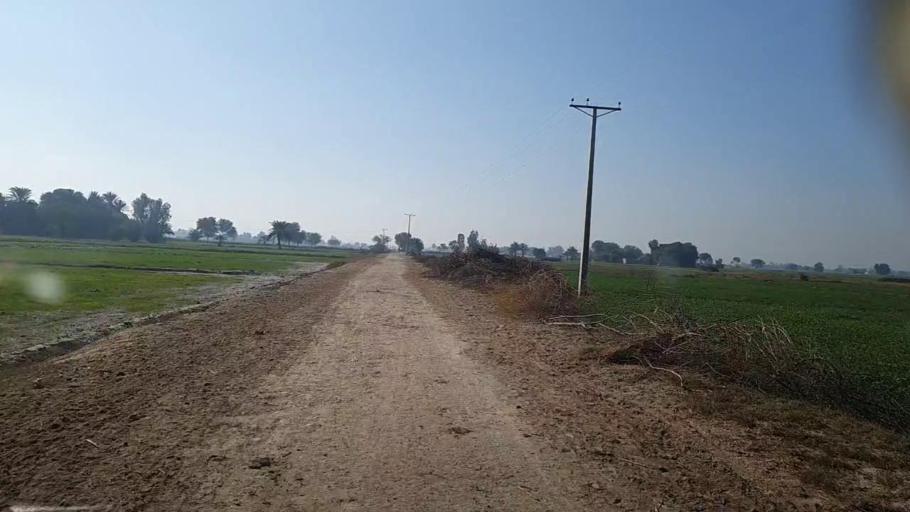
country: PK
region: Sindh
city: Khairpur
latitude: 27.9340
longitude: 69.6966
